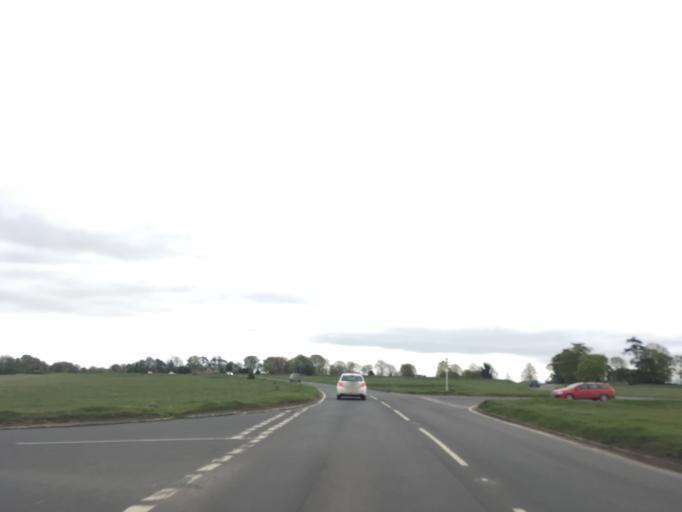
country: GB
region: England
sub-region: Gloucestershire
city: Nailsworth
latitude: 51.7105
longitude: -2.2064
